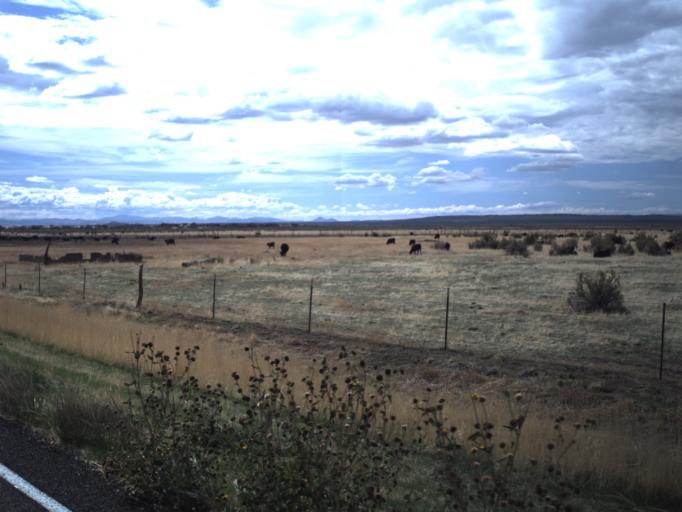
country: US
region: Utah
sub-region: Millard County
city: Fillmore
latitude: 39.1427
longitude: -112.4098
